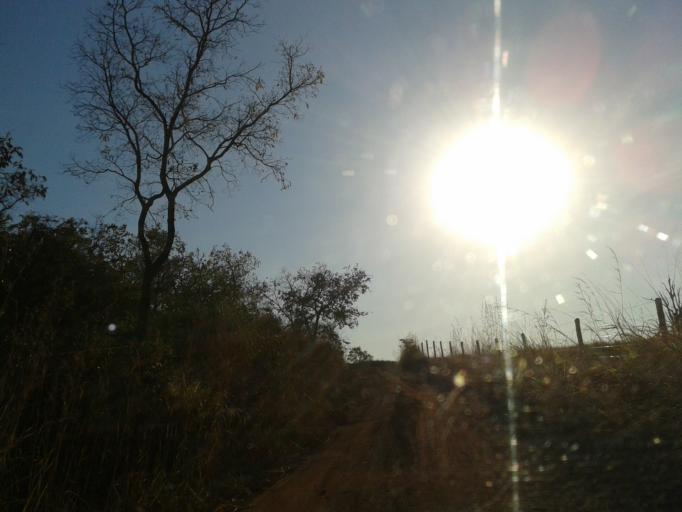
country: BR
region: Minas Gerais
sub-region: Santa Vitoria
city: Santa Vitoria
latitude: -19.1883
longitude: -50.0322
